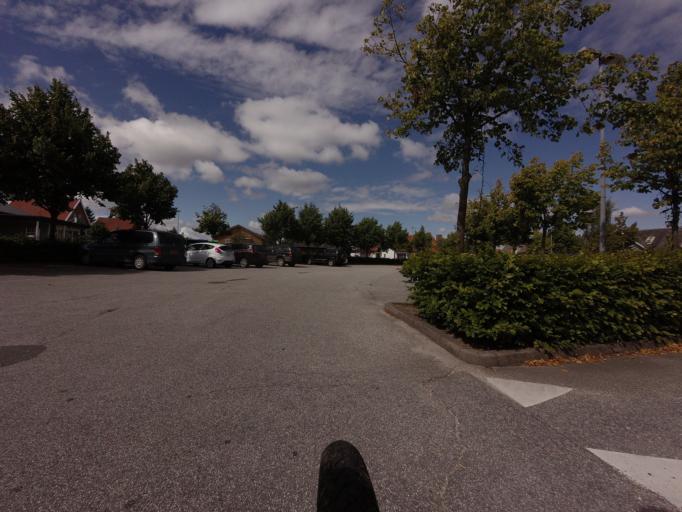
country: DK
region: Central Jutland
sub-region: Norddjurs Kommune
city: Auning
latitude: 56.4298
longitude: 10.3757
